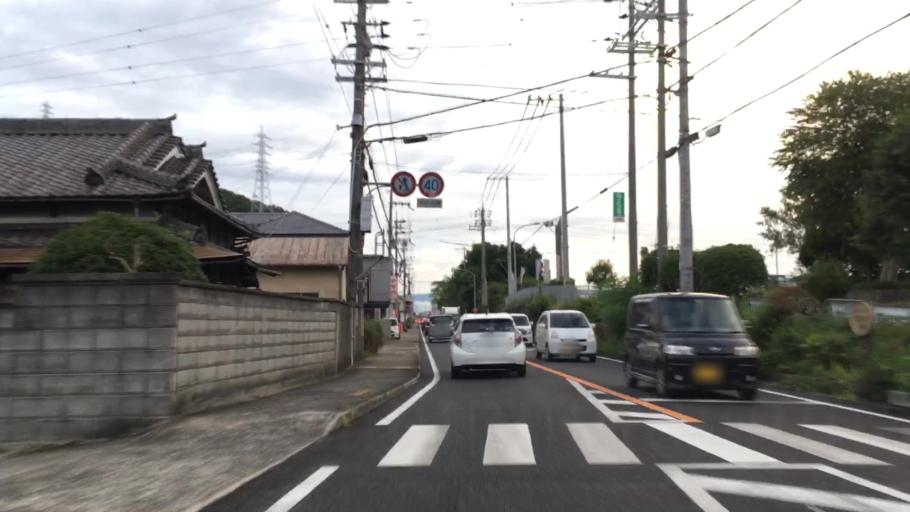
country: JP
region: Hyogo
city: Himeji
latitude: 34.8879
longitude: 134.7297
